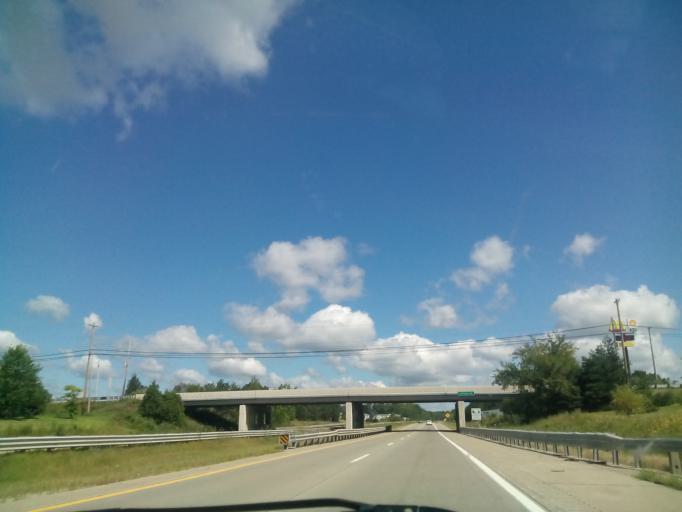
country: US
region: Michigan
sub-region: Genesee County
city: Lake Fenton
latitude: 42.9137
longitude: -83.7258
